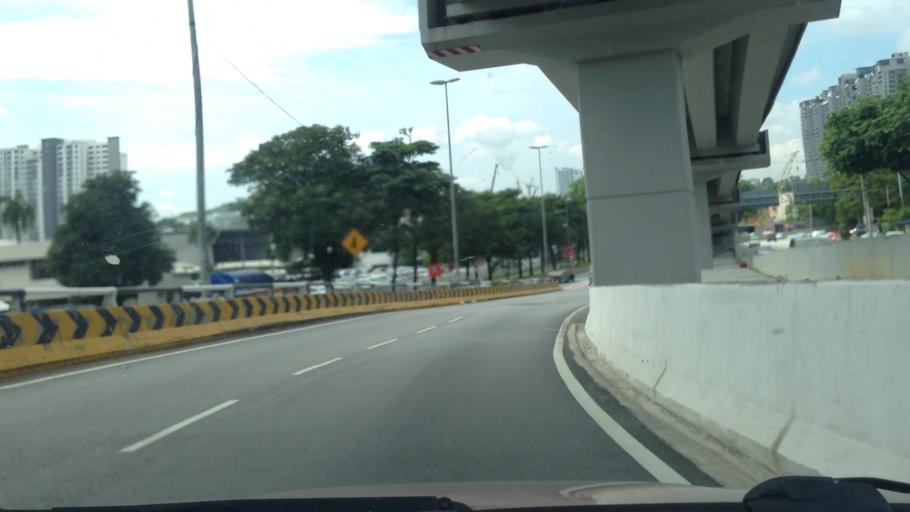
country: MY
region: Kuala Lumpur
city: Kuala Lumpur
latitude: 3.0915
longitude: 101.6914
